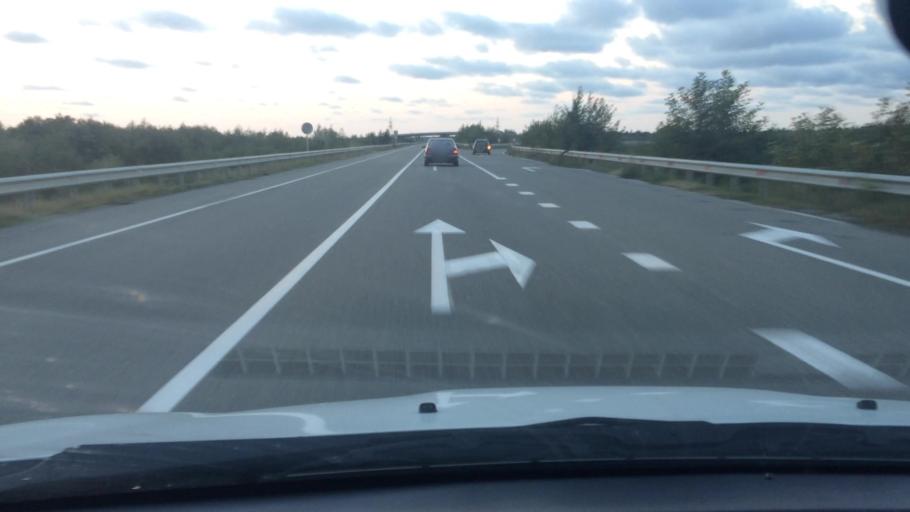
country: GE
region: Ajaria
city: Ochkhamuri
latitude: 41.8942
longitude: 41.8026
